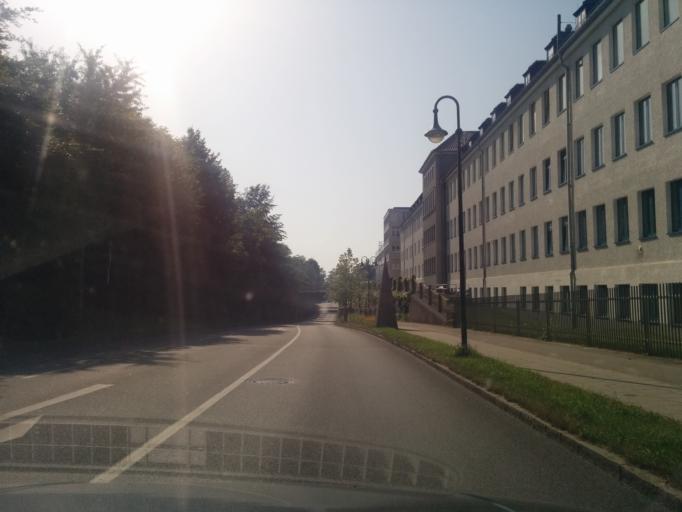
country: DE
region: Bavaria
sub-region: Upper Bavaria
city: Grunwald
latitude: 48.0448
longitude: 11.5073
